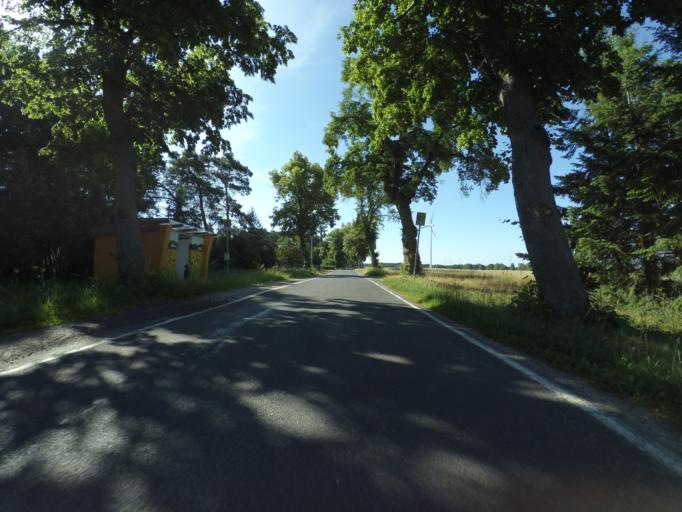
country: DE
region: Brandenburg
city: Putlitz
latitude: 53.3430
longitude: 12.0420
